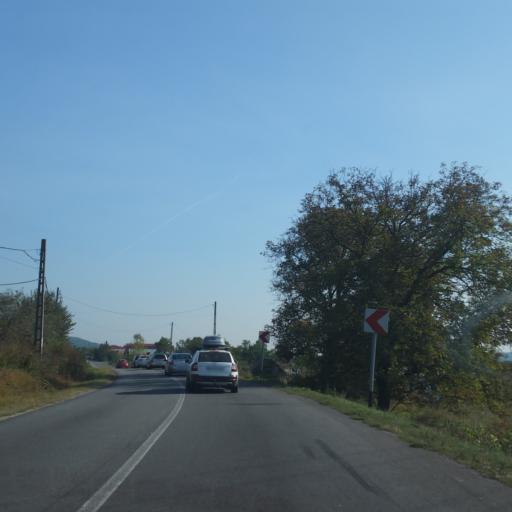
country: RO
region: Arges
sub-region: Comuna Baiculesti
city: Baiculesti
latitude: 45.0234
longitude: 24.7099
